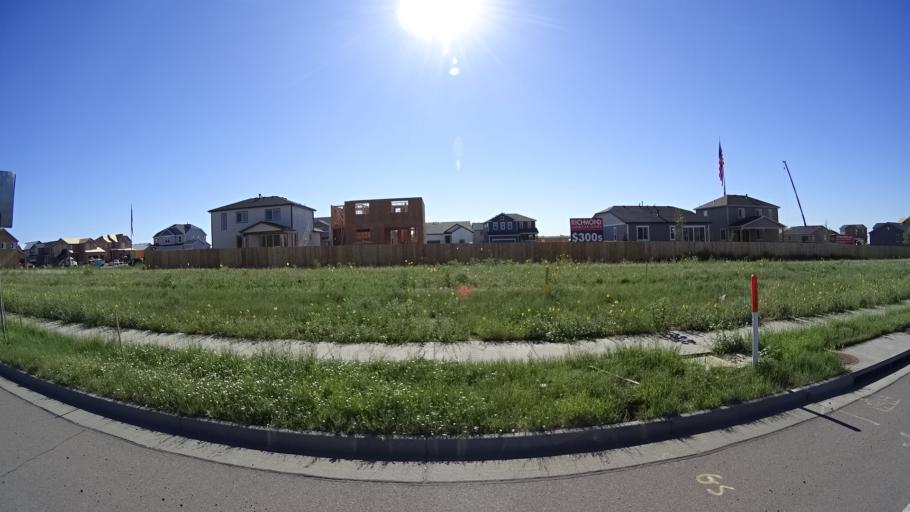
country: US
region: Colorado
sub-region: El Paso County
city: Cimarron Hills
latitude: 38.8707
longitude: -104.6827
